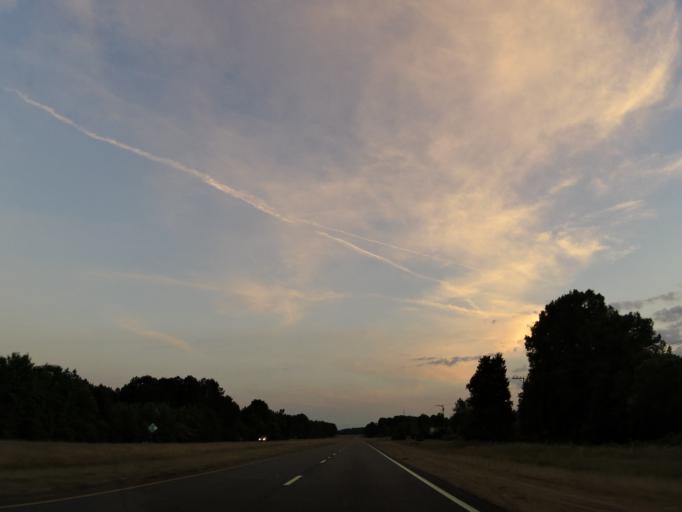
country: US
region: Mississippi
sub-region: Kemper County
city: De Kalb
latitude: 32.6970
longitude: -88.4858
